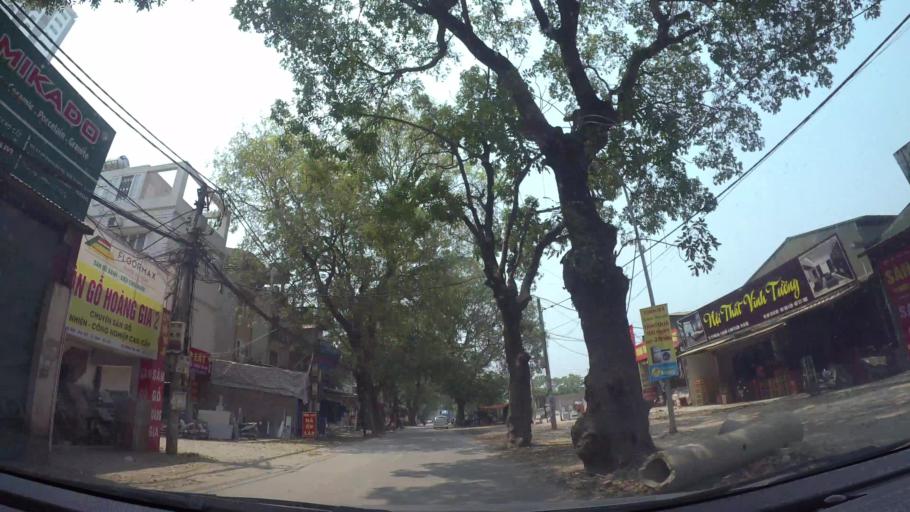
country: VN
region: Ha Noi
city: Ha Dong
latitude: 20.9864
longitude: 105.7676
